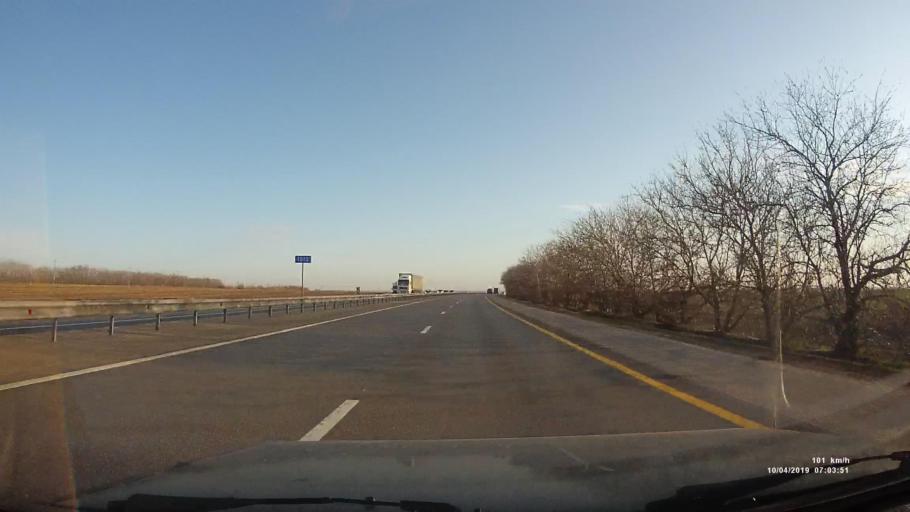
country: RU
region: Rostov
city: Mayskiy
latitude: 47.6289
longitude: 39.9957
